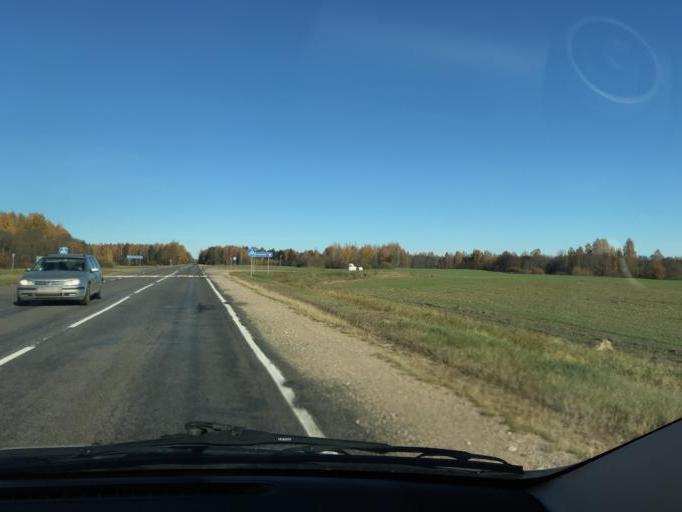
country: BY
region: Vitebsk
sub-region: Ushatski Rayon
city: Ushachy
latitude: 55.0853
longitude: 28.7559
